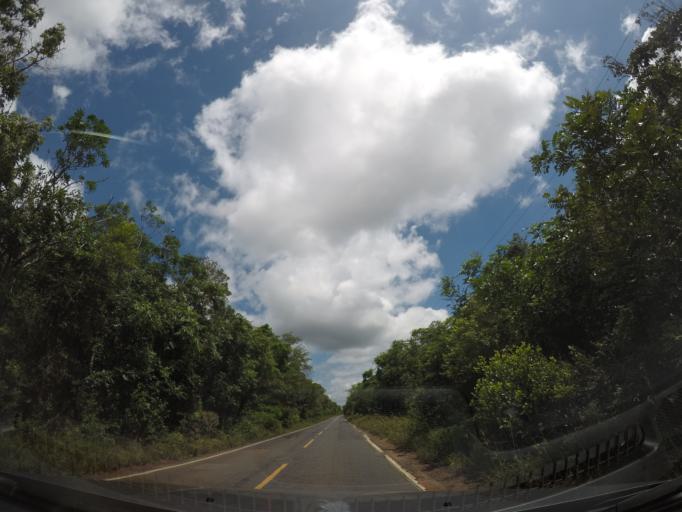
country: BR
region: Bahia
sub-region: Andarai
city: Vera Cruz
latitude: -12.5184
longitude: -41.3628
